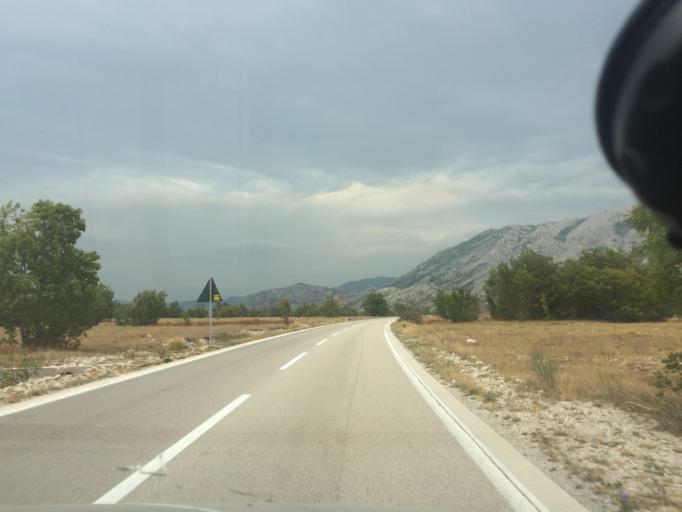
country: ME
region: Kotor
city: Risan
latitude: 42.5861
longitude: 18.6864
